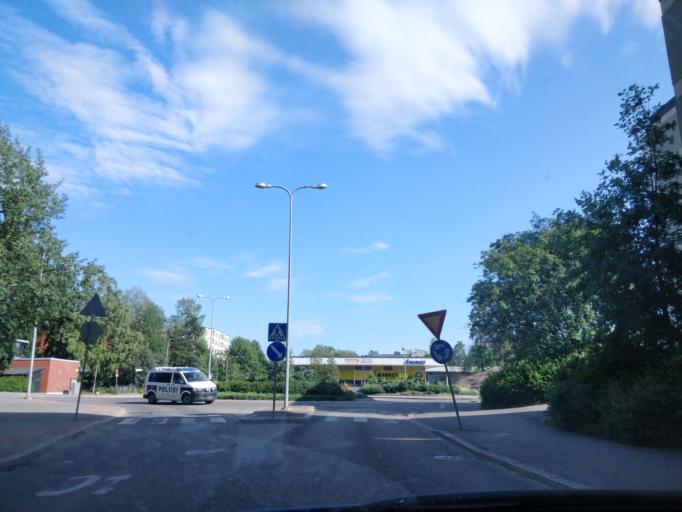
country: FI
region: Uusimaa
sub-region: Helsinki
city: Vantaa
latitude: 60.2353
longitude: 25.0098
